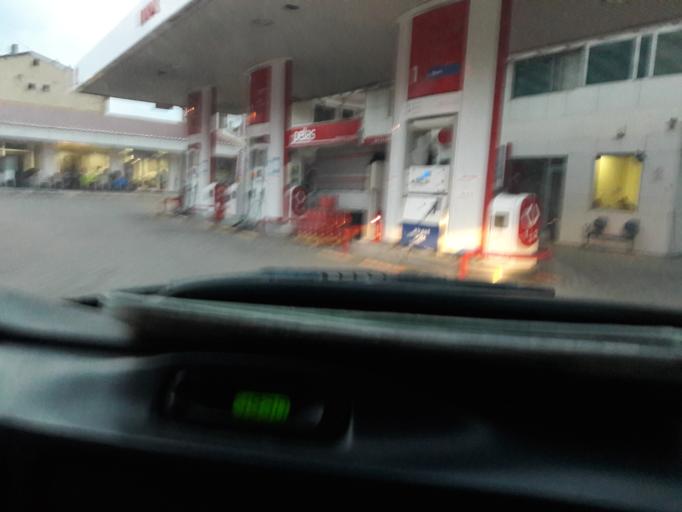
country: TR
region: Giresun
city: Alucra
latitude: 40.3228
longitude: 38.7613
